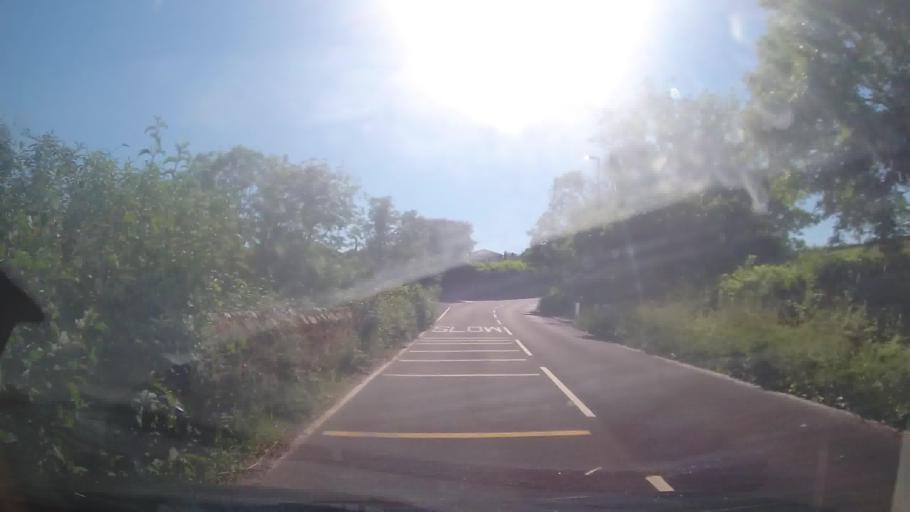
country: GB
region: England
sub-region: Borough of Torbay
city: Brixham
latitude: 50.3755
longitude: -3.5372
